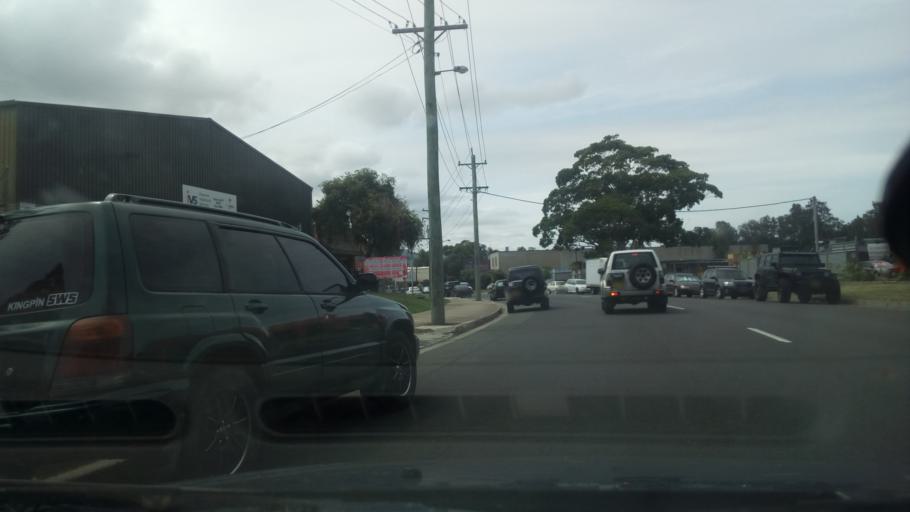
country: AU
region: New South Wales
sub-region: Wollongong
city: Gwynneville
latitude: -34.4082
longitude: 150.8951
